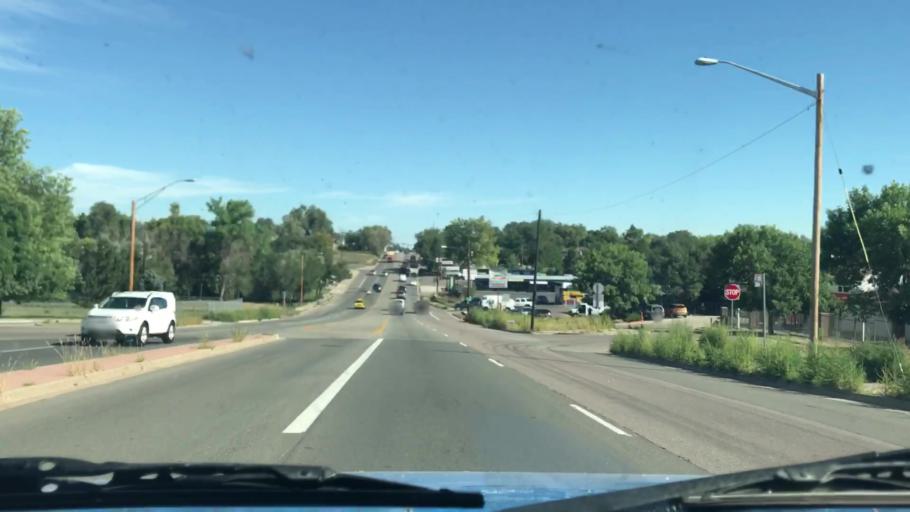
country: US
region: Colorado
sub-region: Jefferson County
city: Edgewater
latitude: 39.7269
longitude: -105.0532
